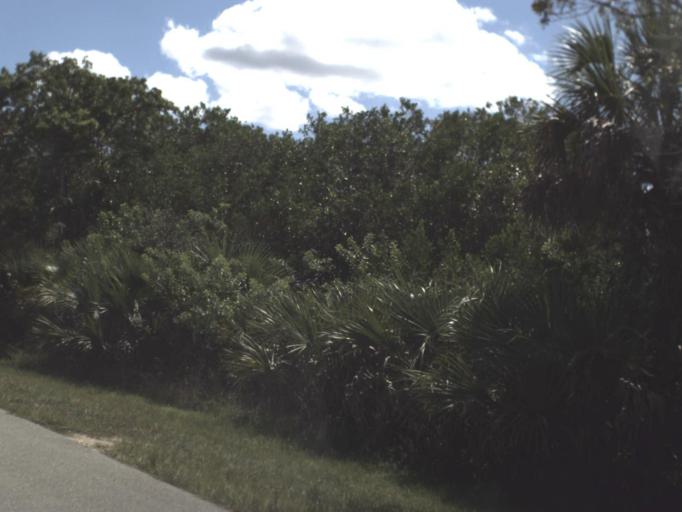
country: US
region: Florida
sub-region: Collier County
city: Marco
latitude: 25.9893
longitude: -81.5861
